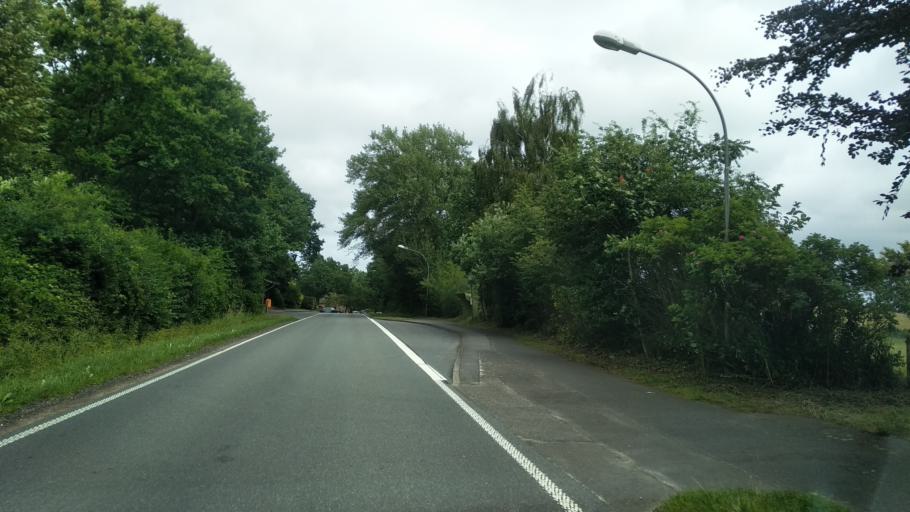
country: DE
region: Schleswig-Holstein
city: Neuberend
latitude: 54.5471
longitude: 9.5357
